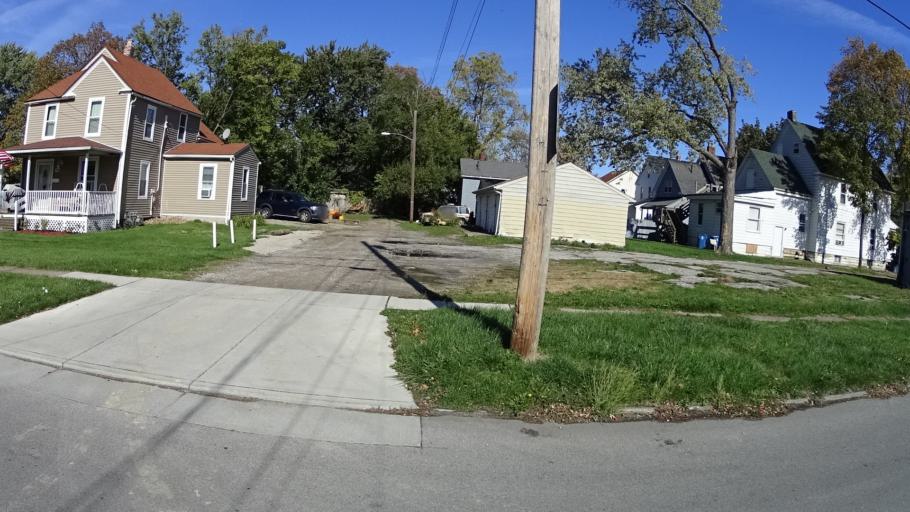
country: US
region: Ohio
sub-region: Lorain County
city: Lorain
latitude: 41.4599
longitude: -82.1798
